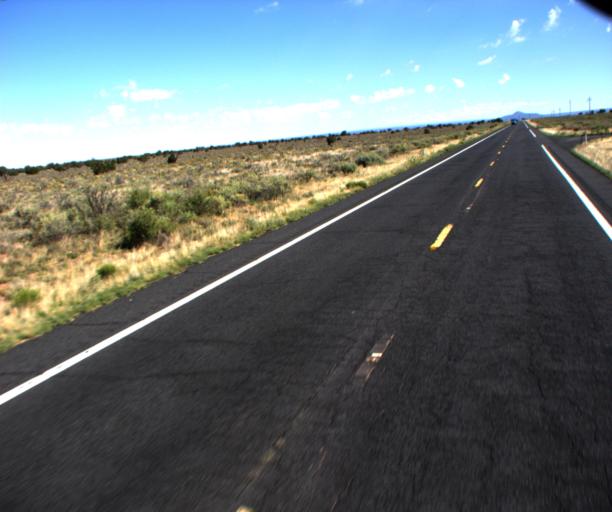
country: US
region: Arizona
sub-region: Coconino County
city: Williams
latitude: 35.5957
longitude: -112.1484
